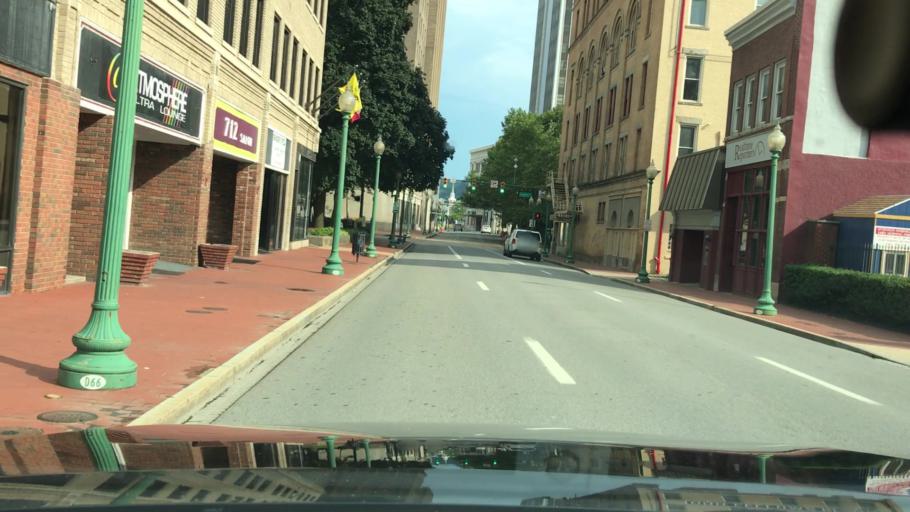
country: US
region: West Virginia
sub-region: Kanawha County
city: Charleston
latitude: 38.3515
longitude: -81.6338
